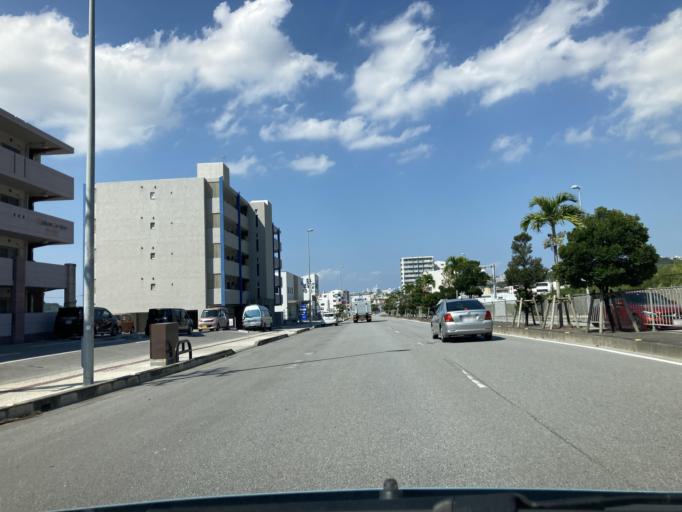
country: JP
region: Okinawa
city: Tomigusuku
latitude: 26.1889
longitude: 127.7177
